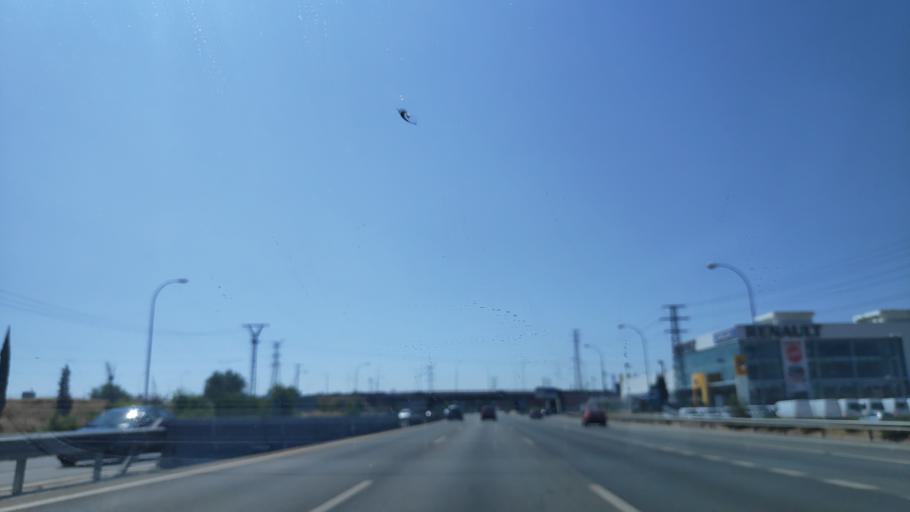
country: ES
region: Madrid
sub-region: Provincia de Madrid
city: Getafe
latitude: 40.3337
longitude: -3.7249
